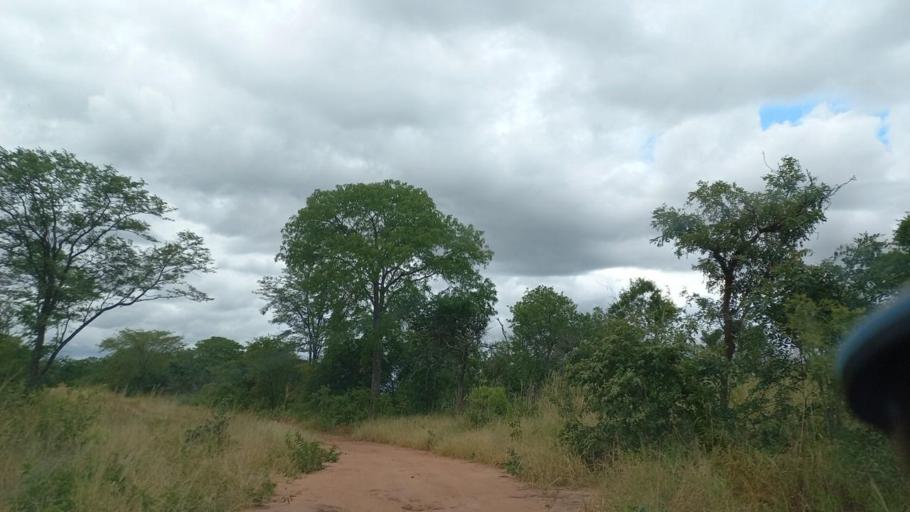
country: ZM
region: Lusaka
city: Luangwa
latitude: -15.5694
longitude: 30.3209
